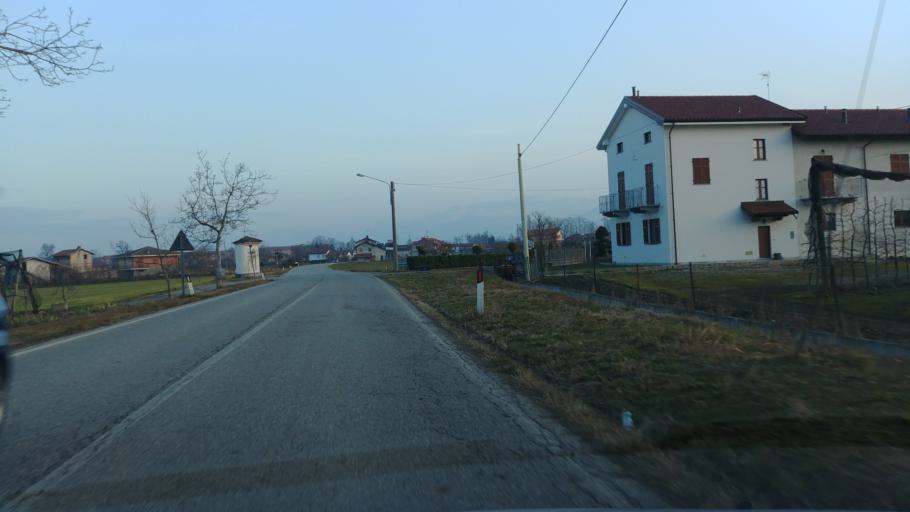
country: IT
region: Piedmont
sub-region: Provincia di Cuneo
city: Cuneo
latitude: 44.4063
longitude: 7.5213
